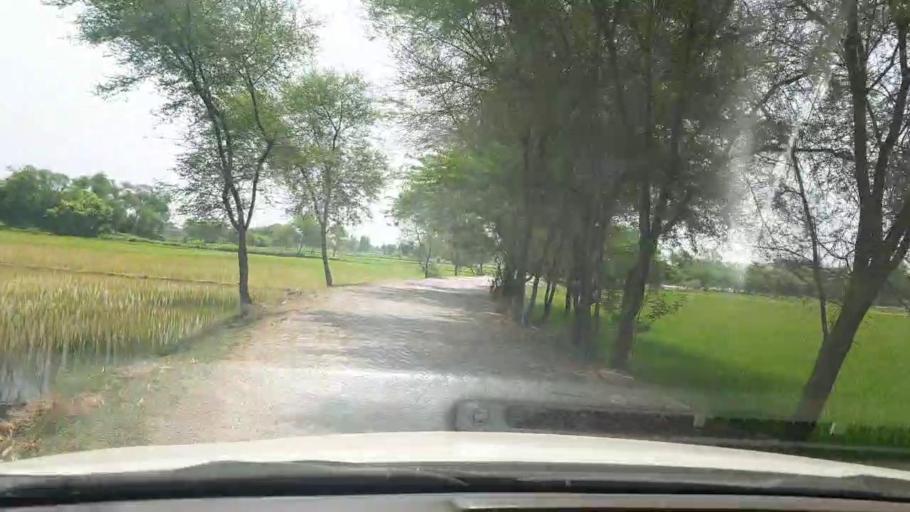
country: PK
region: Sindh
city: Shikarpur
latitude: 28.0210
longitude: 68.6465
